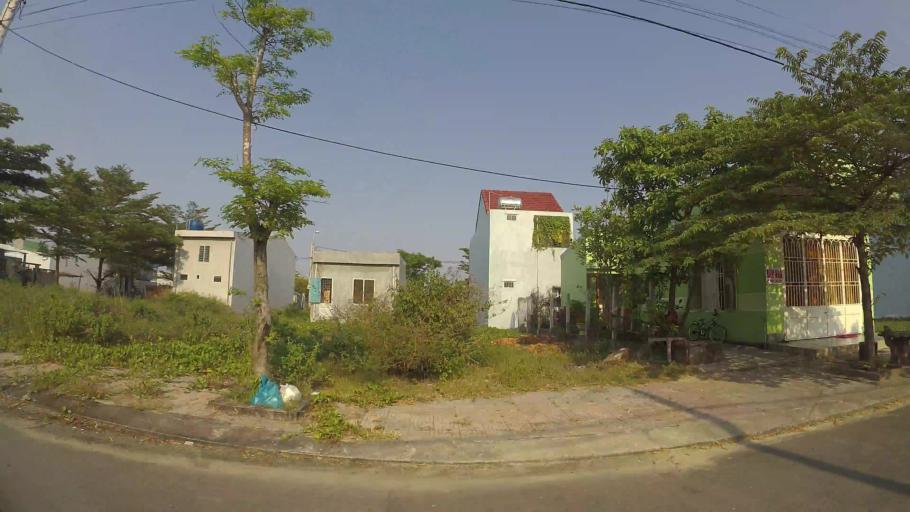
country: VN
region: Quang Nam
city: Quang Nam
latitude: 15.9469
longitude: 108.2579
